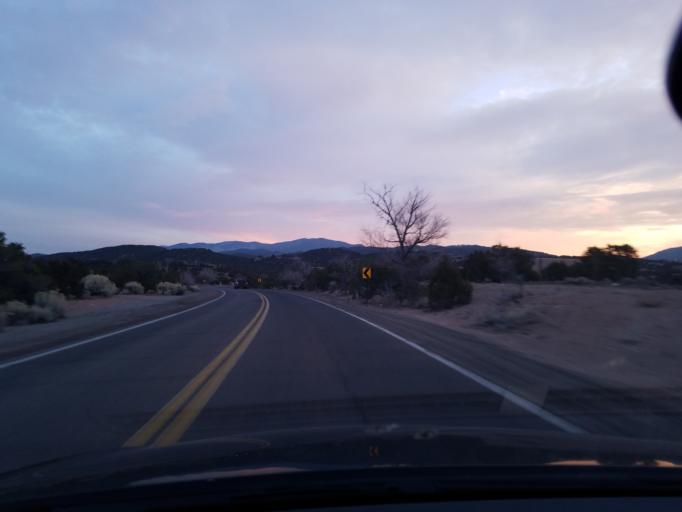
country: US
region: New Mexico
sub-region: Santa Fe County
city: Santa Fe
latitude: 35.6935
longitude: -105.9209
